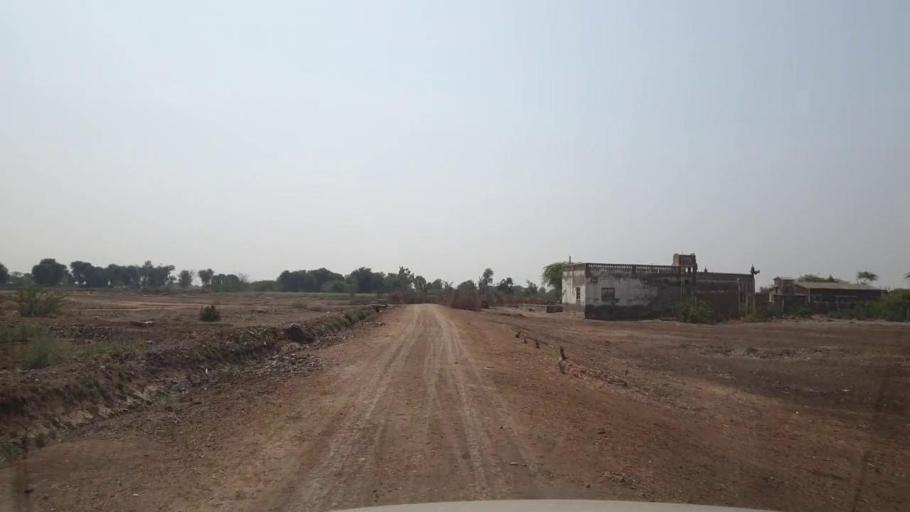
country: PK
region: Sindh
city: Chor
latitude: 25.4538
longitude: 69.6797
